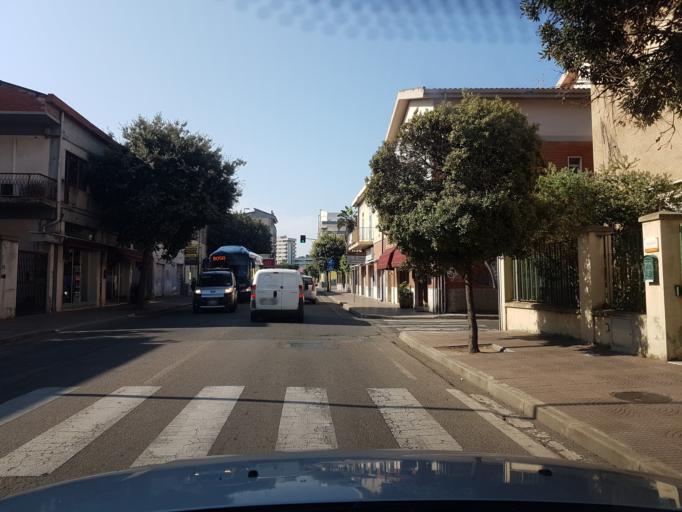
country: IT
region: Sardinia
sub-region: Provincia di Oristano
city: Oristano
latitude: 39.9054
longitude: 8.5883
